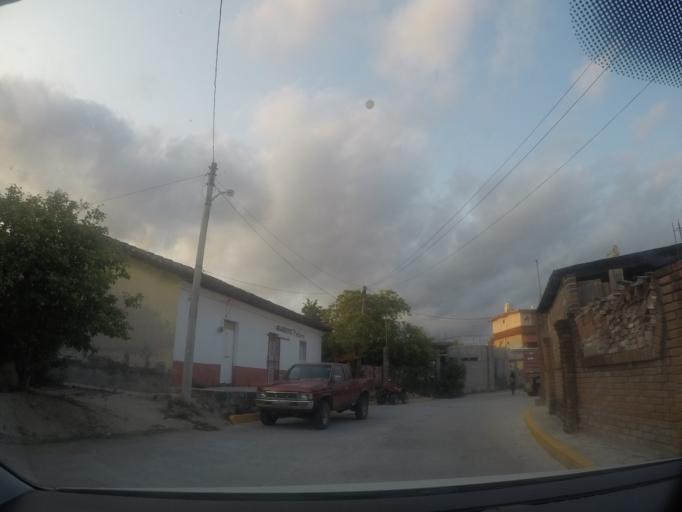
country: MX
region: Oaxaca
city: San Jeronimo Ixtepec
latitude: 16.5842
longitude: -95.2062
